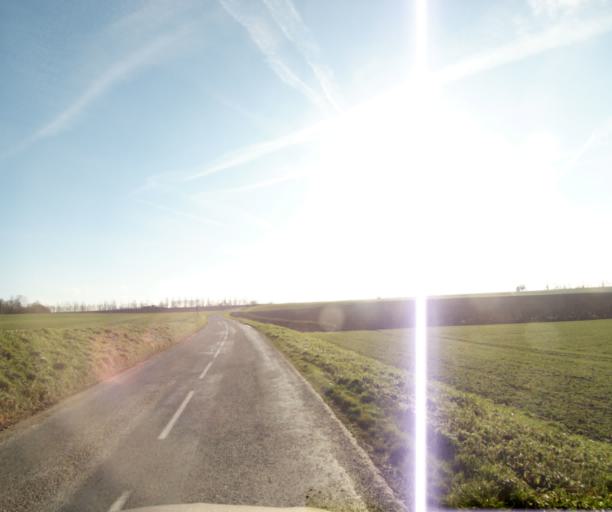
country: FR
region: Nord-Pas-de-Calais
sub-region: Departement du Nord
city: Saultain
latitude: 50.3253
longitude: 3.5746
